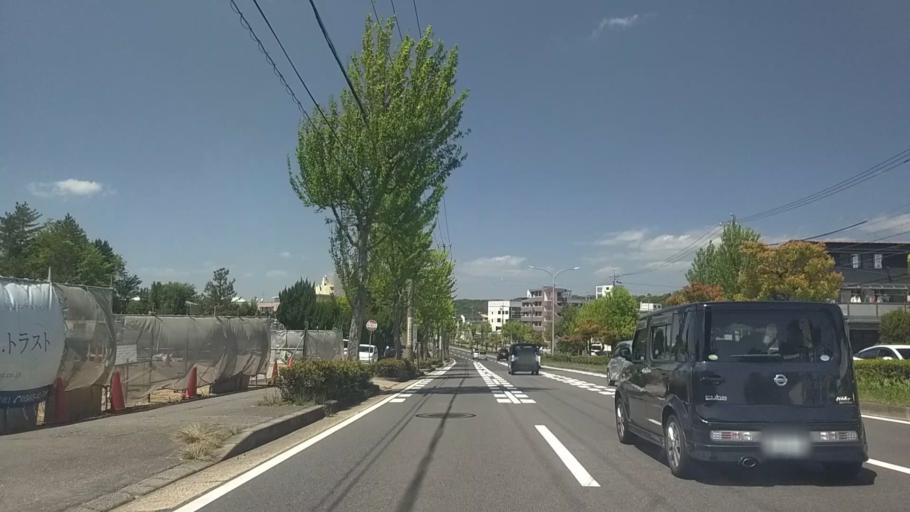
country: JP
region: Aichi
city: Okazaki
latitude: 34.9555
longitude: 137.1898
